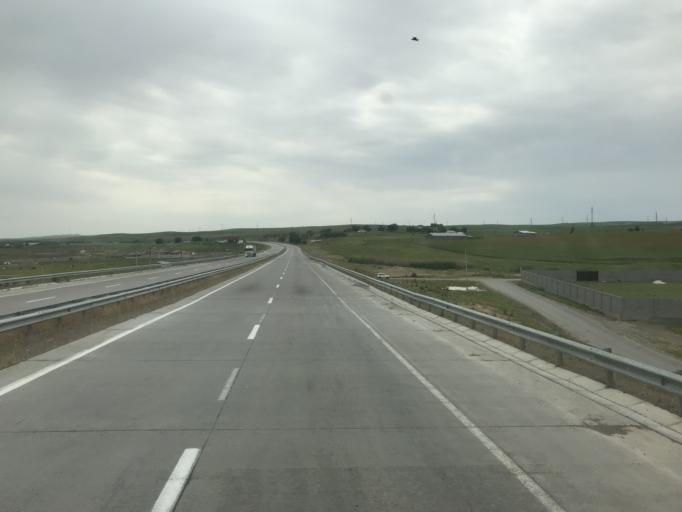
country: KZ
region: Ongtustik Qazaqstan
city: Qazyqurt
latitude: 41.8701
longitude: 69.4209
